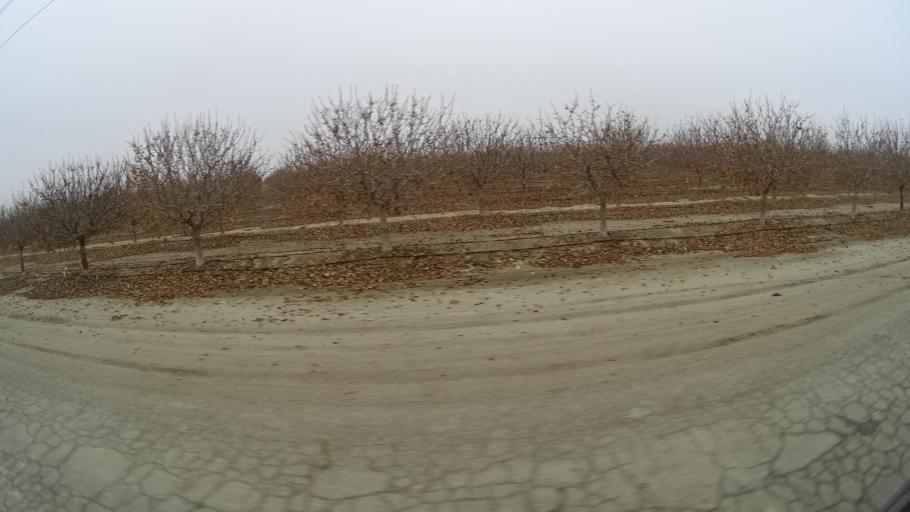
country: US
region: California
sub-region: Tulare County
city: Alpaugh
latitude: 35.7747
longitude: -119.4012
